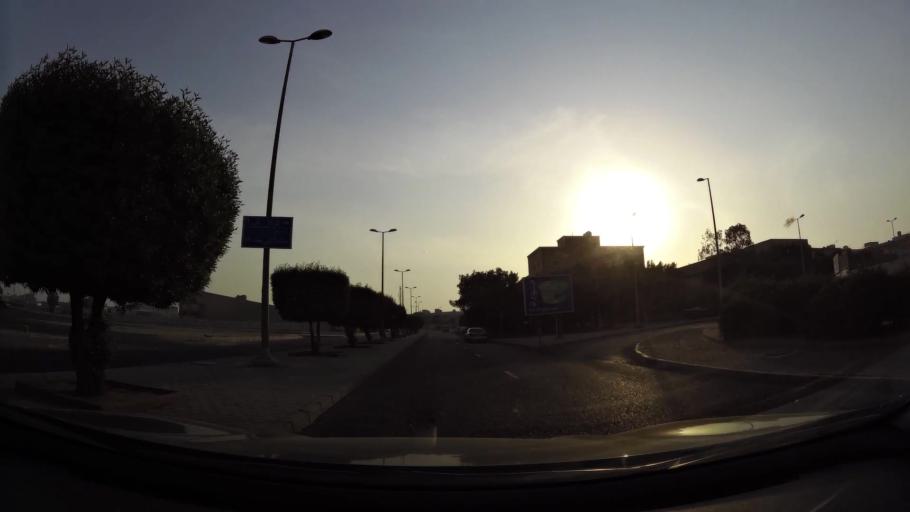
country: KW
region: Mubarak al Kabir
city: Sabah as Salim
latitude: 29.2454
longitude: 48.0626
